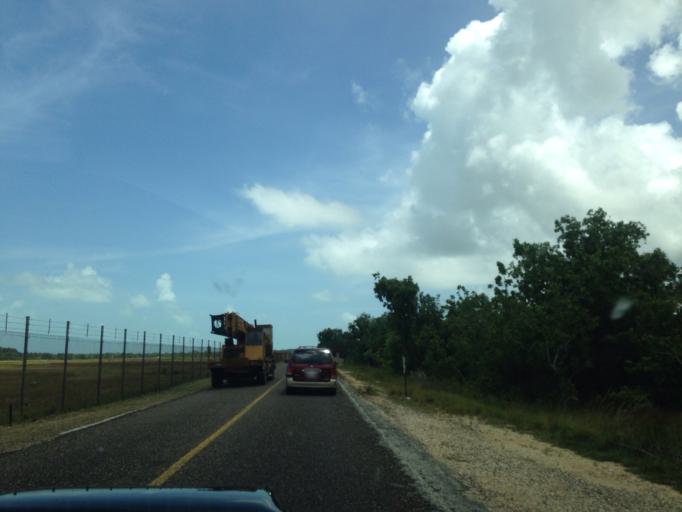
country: BZ
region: Belize
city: Belize City
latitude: 17.5384
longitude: -88.3007
